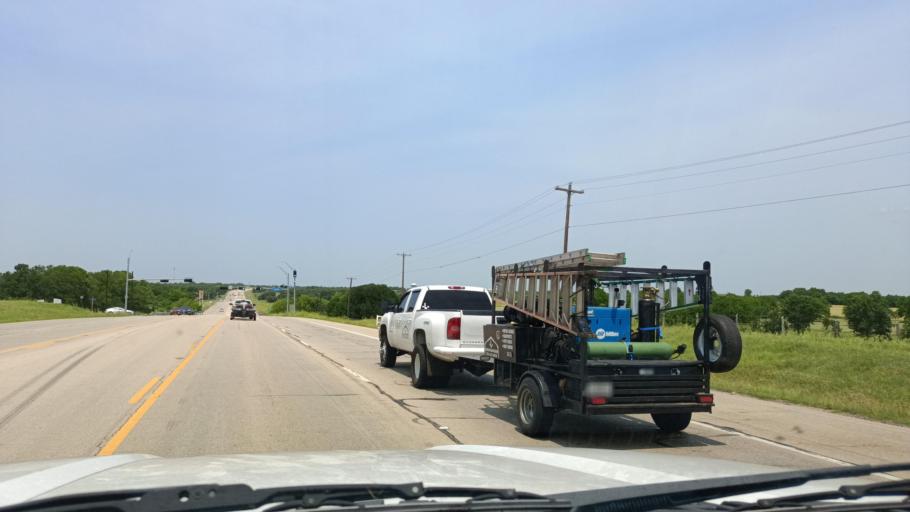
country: US
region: Texas
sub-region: Bell County
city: Temple
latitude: 31.1251
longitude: -97.3934
